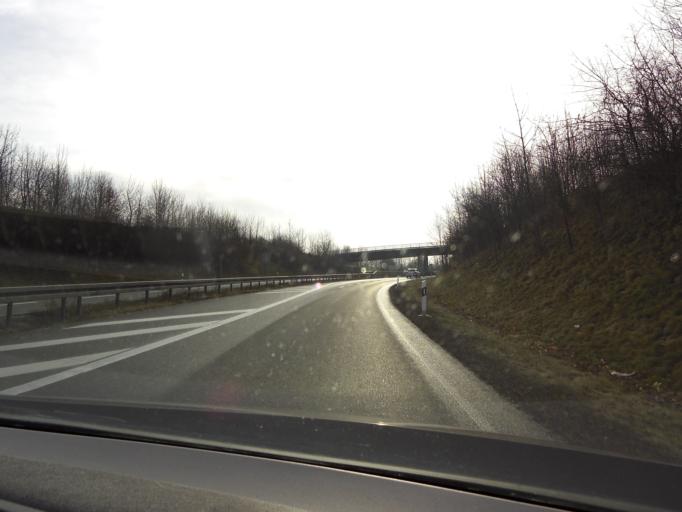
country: DE
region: Thuringia
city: Hopfgarten
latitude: 50.9804
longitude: 11.2917
